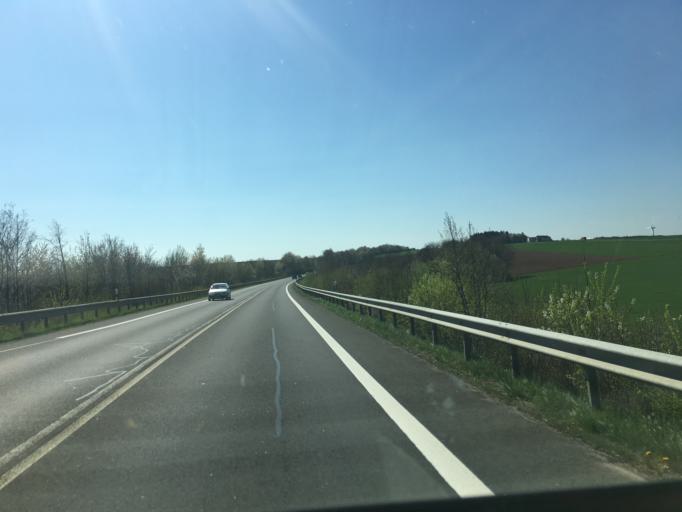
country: DE
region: Rheinland-Pfalz
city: Fliessem
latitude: 50.0121
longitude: 6.5372
